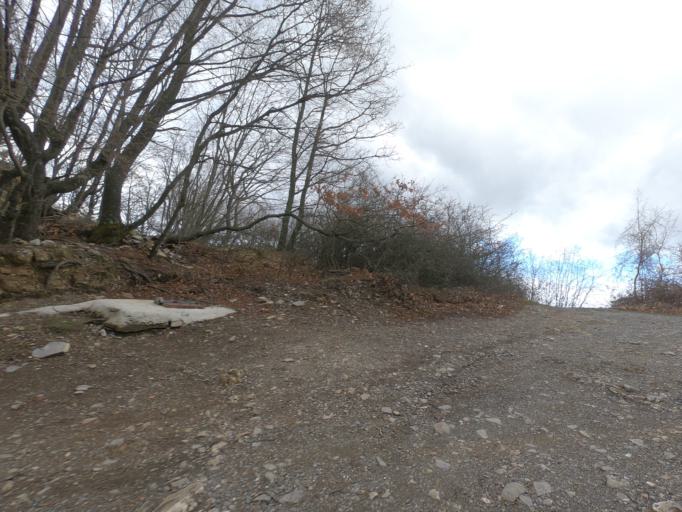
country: IT
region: Liguria
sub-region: Provincia di Imperia
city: Pietrabruna
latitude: 43.9113
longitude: 7.8954
